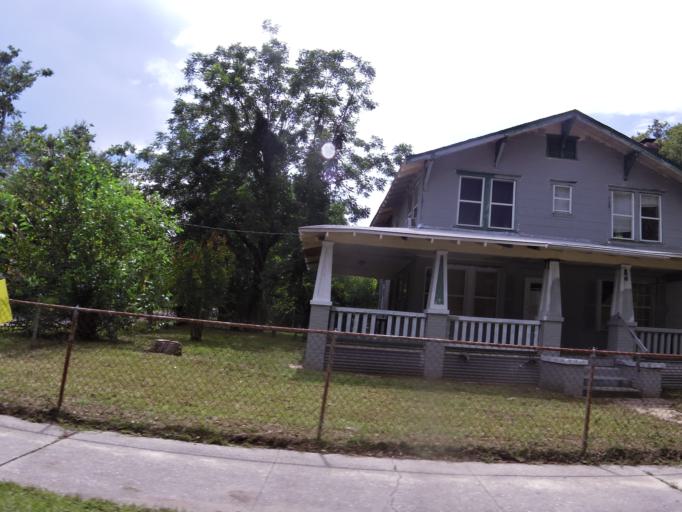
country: US
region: Florida
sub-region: Duval County
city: Jacksonville
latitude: 30.3800
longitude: -81.6415
